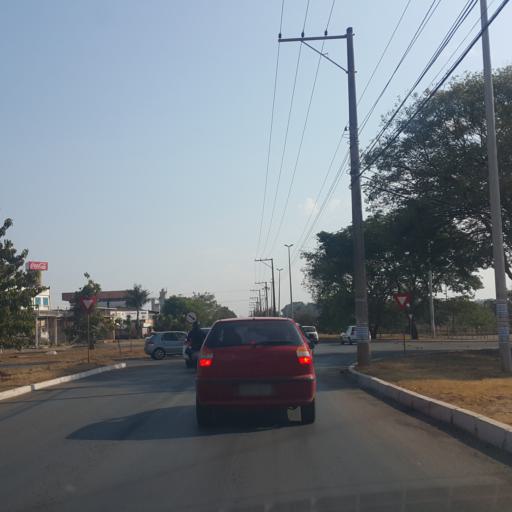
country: BR
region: Federal District
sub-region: Brasilia
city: Brasilia
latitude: -15.8677
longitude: -48.0364
